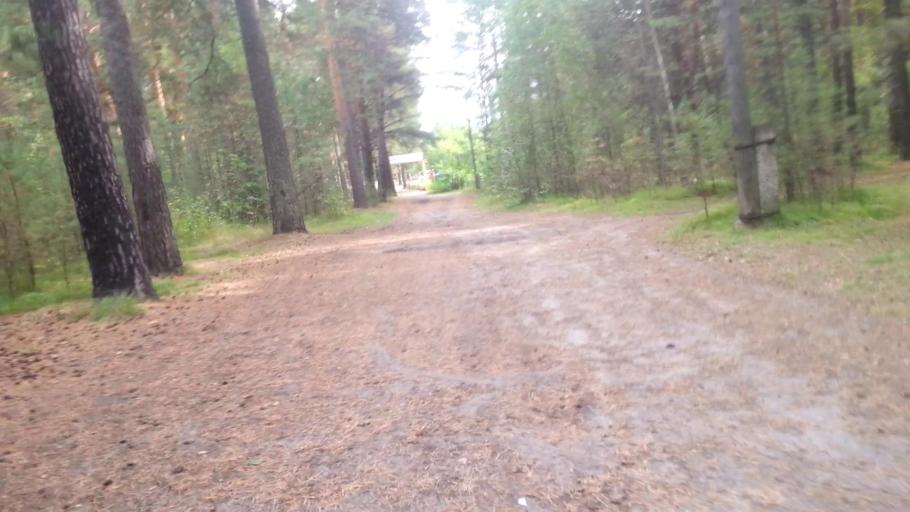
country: RU
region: Altai Krai
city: Yuzhnyy
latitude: 53.3105
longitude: 83.6928
